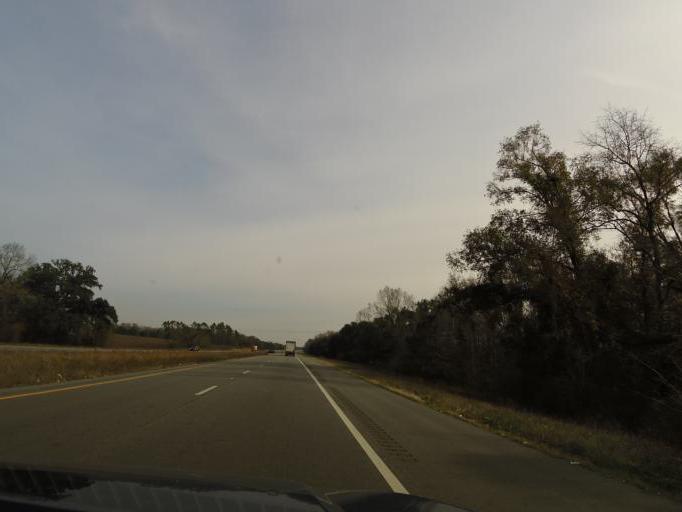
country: US
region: Alabama
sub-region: Houston County
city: Ashford
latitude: 31.1694
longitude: -85.2127
